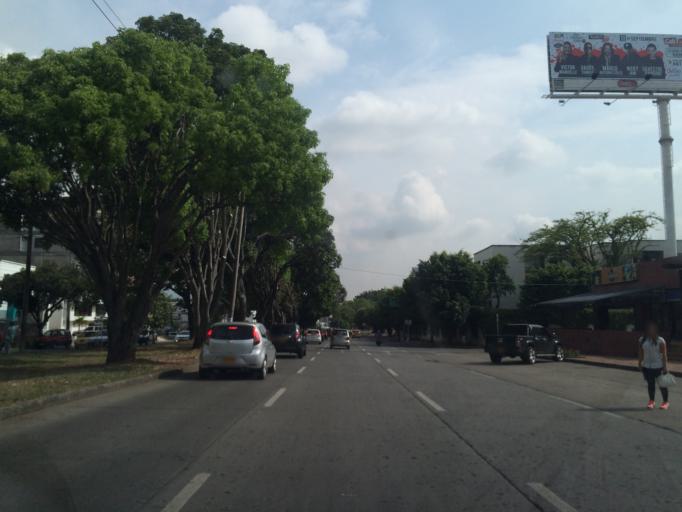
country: CO
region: Valle del Cauca
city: Cali
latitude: 3.3963
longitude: -76.5378
